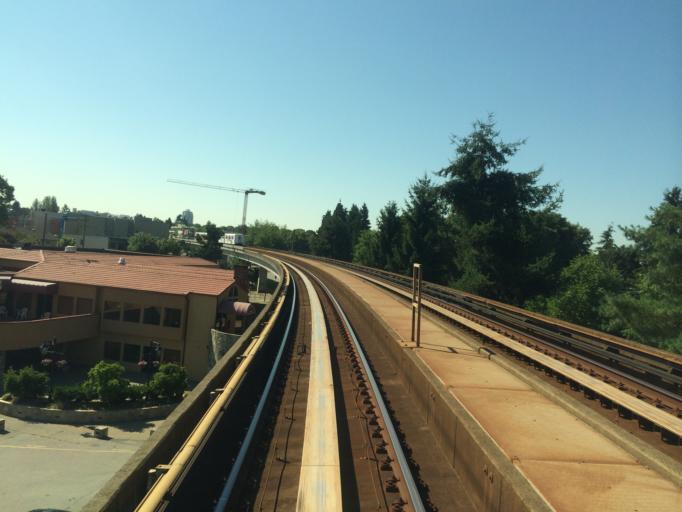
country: CA
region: British Columbia
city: Vancouver
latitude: 49.2557
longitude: -123.0689
